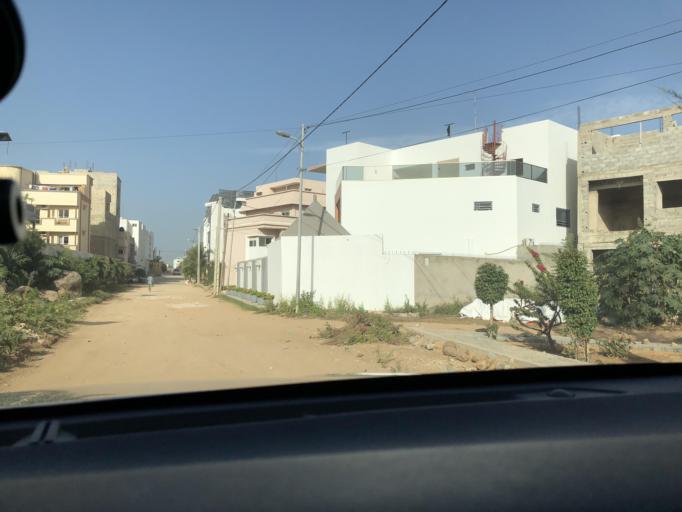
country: SN
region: Dakar
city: Mermoz Boabab
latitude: 14.7321
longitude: -17.4999
